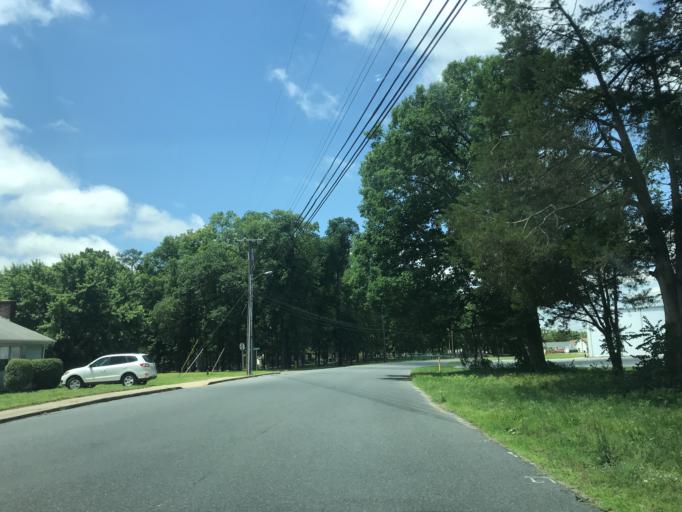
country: US
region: Maryland
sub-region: Caroline County
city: Federalsburg
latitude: 38.6930
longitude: -75.7626
